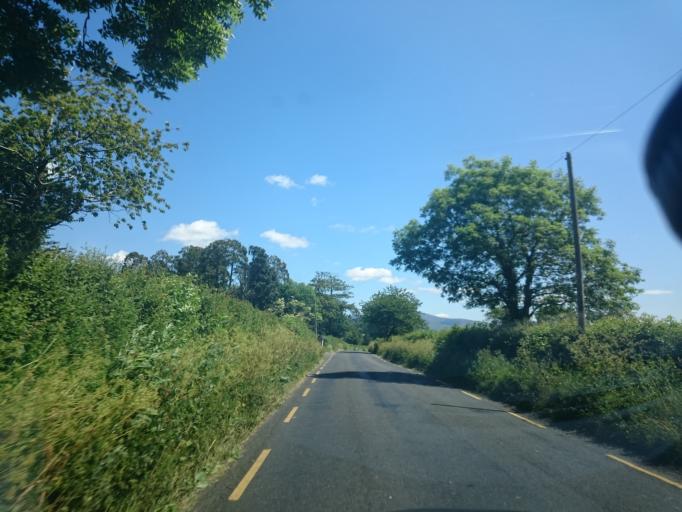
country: IE
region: Leinster
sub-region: Kilkenny
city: Graiguenamanagh
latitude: 52.5927
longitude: -6.9780
